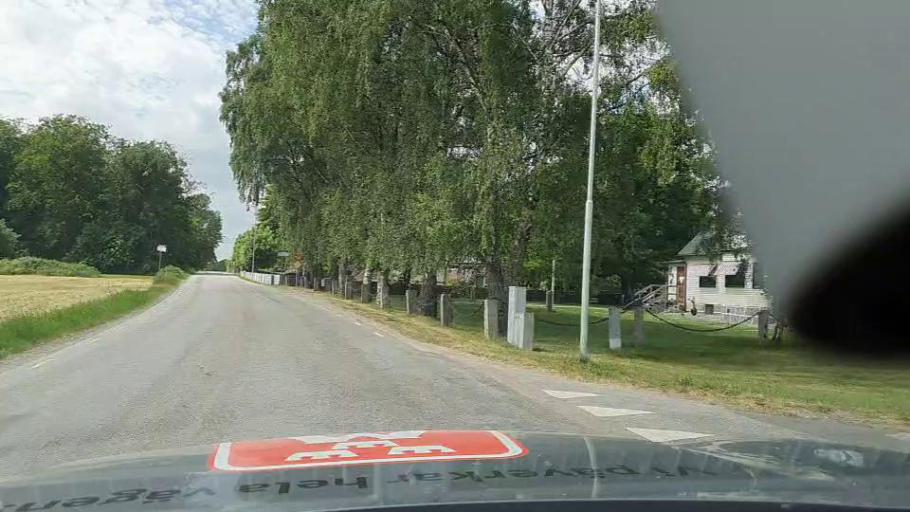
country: SE
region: Blekinge
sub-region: Karlshamns Kommun
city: Morrum
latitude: 56.1112
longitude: 14.6834
